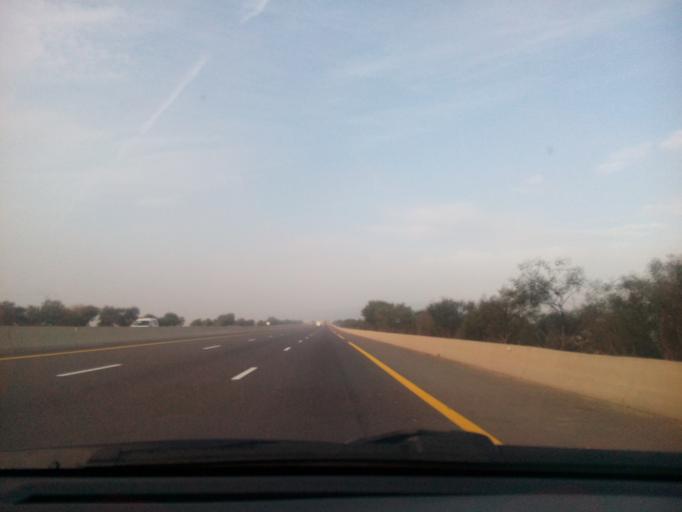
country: DZ
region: Relizane
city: Relizane
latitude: 35.7913
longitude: 0.4578
